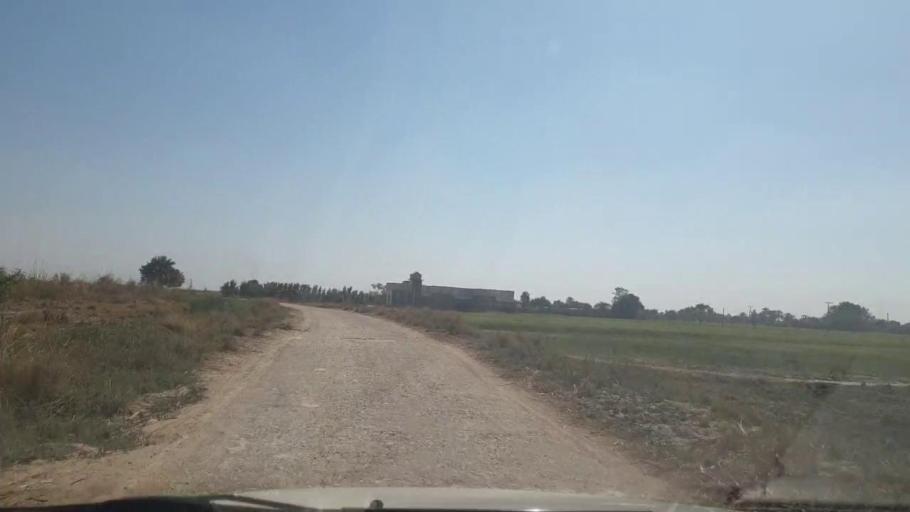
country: PK
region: Sindh
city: Mirpur Khas
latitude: 25.4953
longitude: 69.1366
